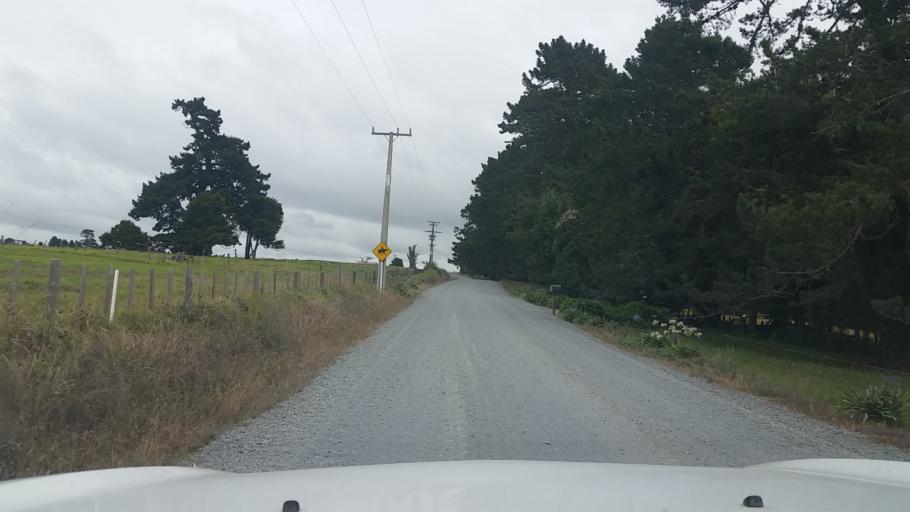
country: NZ
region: Northland
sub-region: Whangarei
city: Maungatapere
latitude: -35.6642
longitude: 174.1814
